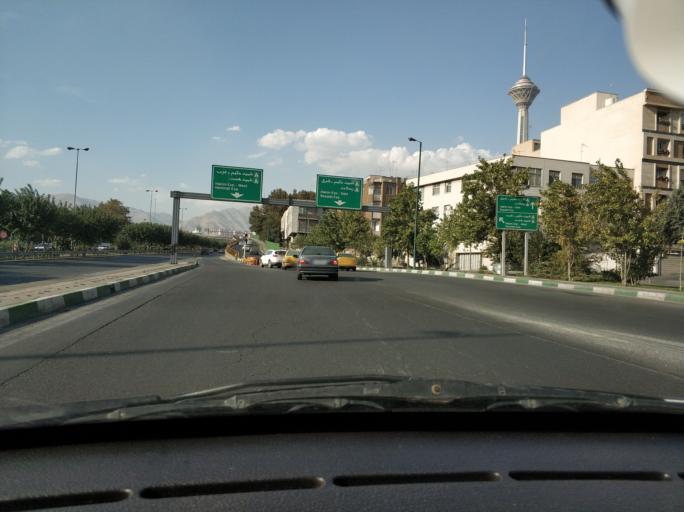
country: IR
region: Tehran
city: Tehran
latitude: 35.7347
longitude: 51.3714
